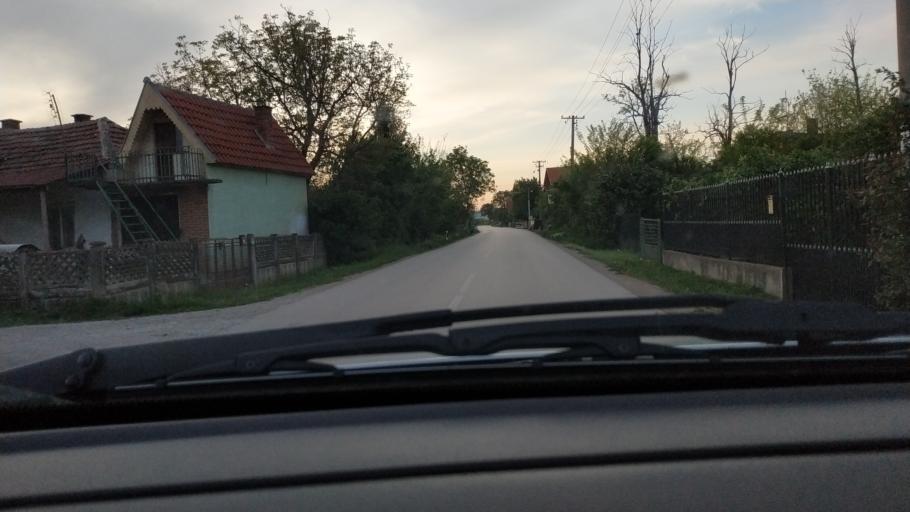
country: RS
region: Central Serbia
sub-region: Nisavski Okrug
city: Aleksinac
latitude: 43.5444
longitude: 21.6261
